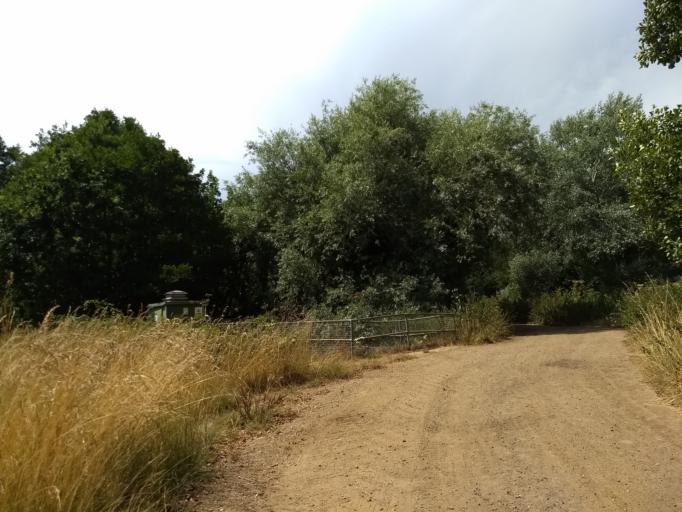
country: GB
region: England
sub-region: Isle of Wight
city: Newchurch
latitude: 50.6490
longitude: -1.2495
